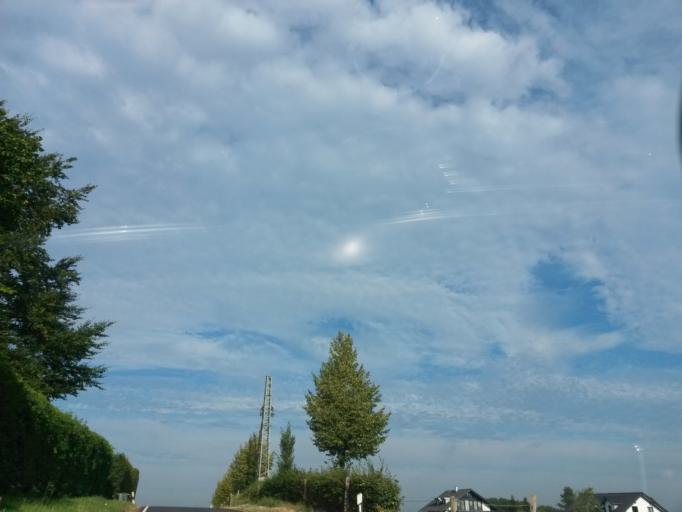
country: DE
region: North Rhine-Westphalia
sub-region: Regierungsbezirk Koln
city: Rosrath
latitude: 50.8900
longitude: 7.2051
